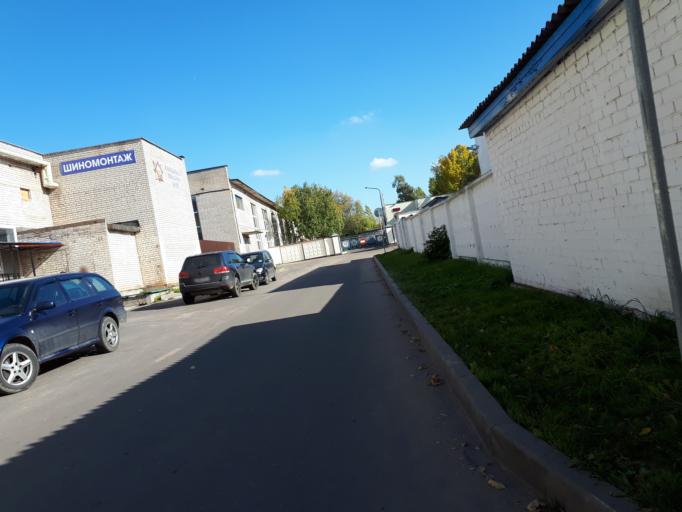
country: BY
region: Vitebsk
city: Vitebsk
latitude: 55.1691
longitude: 30.2437
